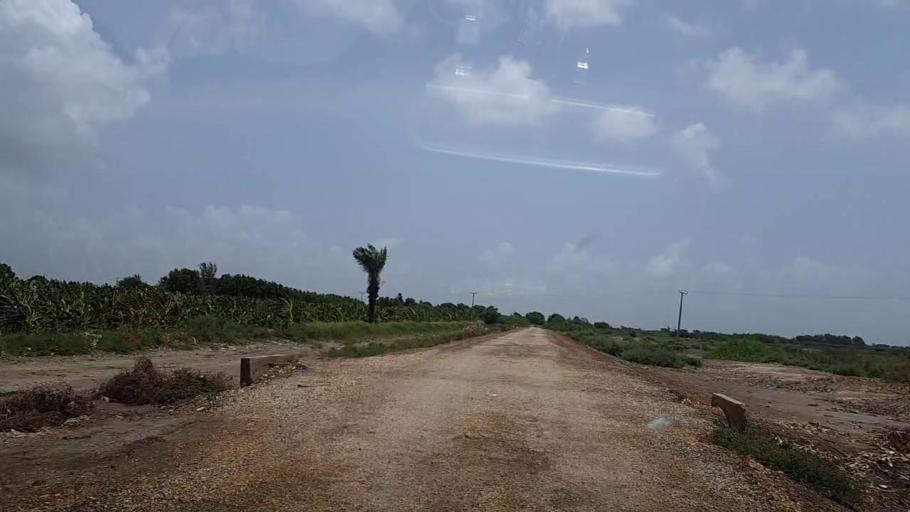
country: PK
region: Sindh
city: Keti Bandar
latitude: 24.1679
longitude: 67.5432
